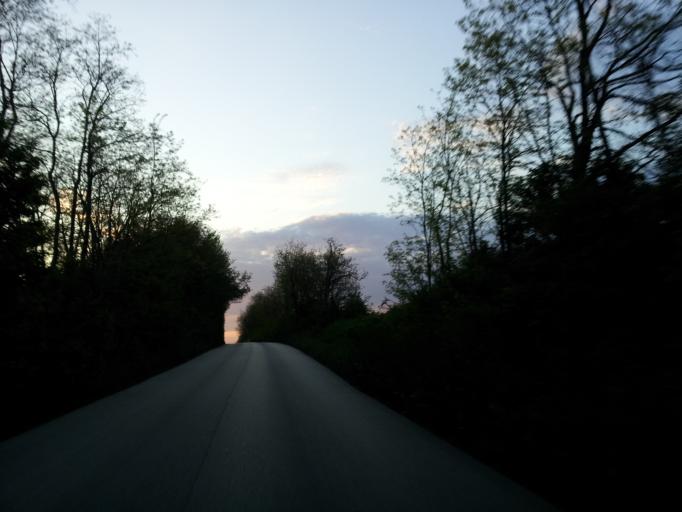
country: HU
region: Pest
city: Perbal
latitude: 47.6245
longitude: 18.7658
